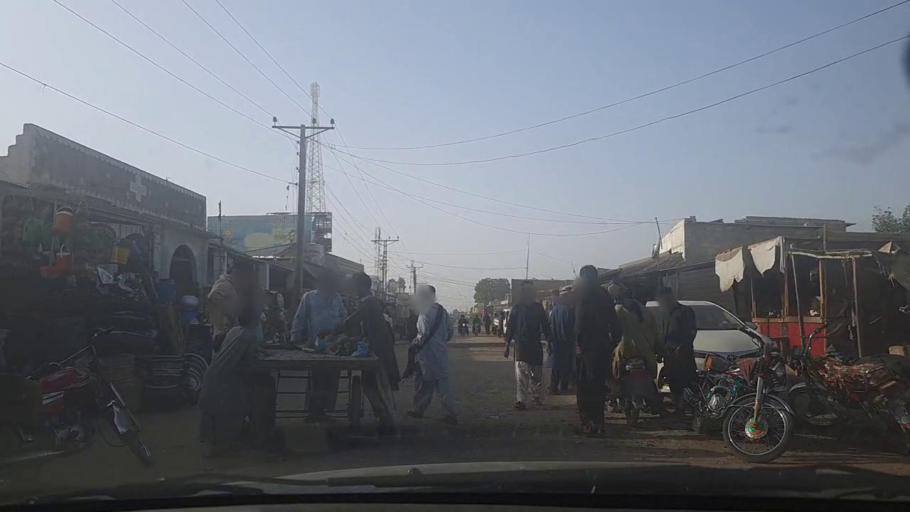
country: PK
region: Sindh
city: Keti Bandar
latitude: 24.3011
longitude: 67.6063
